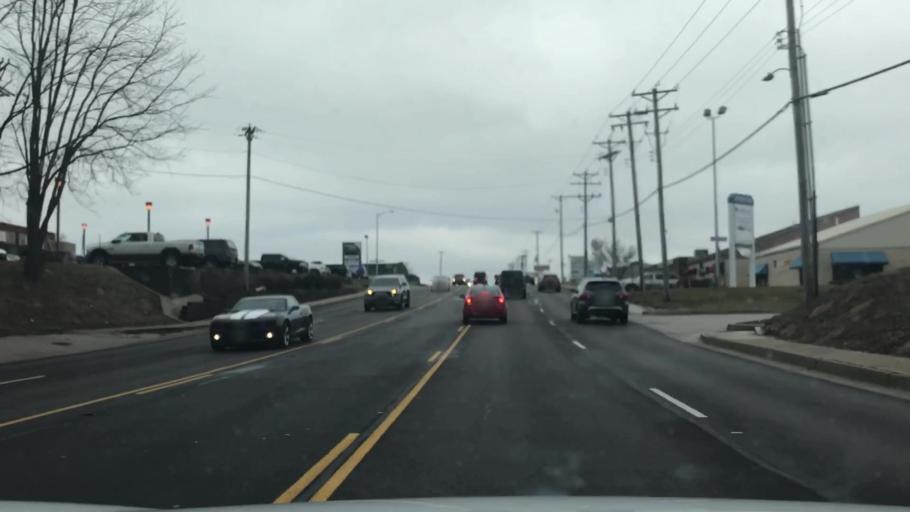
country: US
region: Missouri
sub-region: Saint Charles County
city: Saint Peters
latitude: 38.7911
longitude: -90.5680
